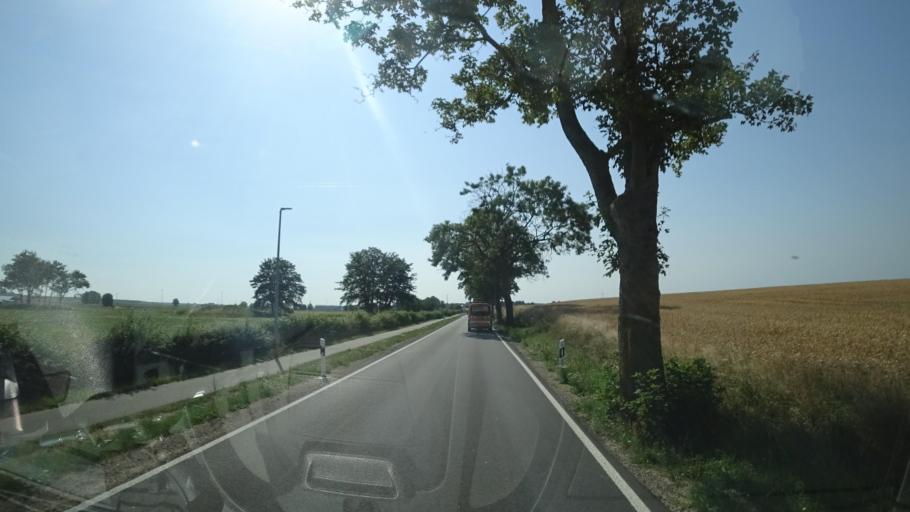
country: DE
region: Mecklenburg-Vorpommern
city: Kroslin
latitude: 54.1280
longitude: 13.7402
